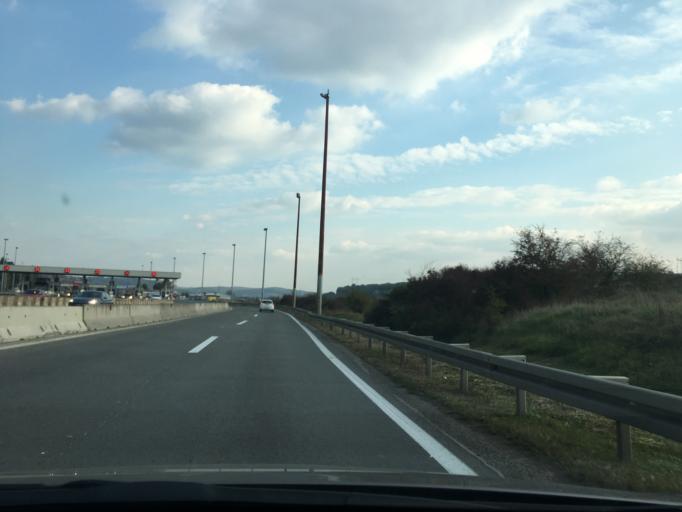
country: RS
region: Central Serbia
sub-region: Belgrade
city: Zvezdara
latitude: 44.7193
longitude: 20.5516
